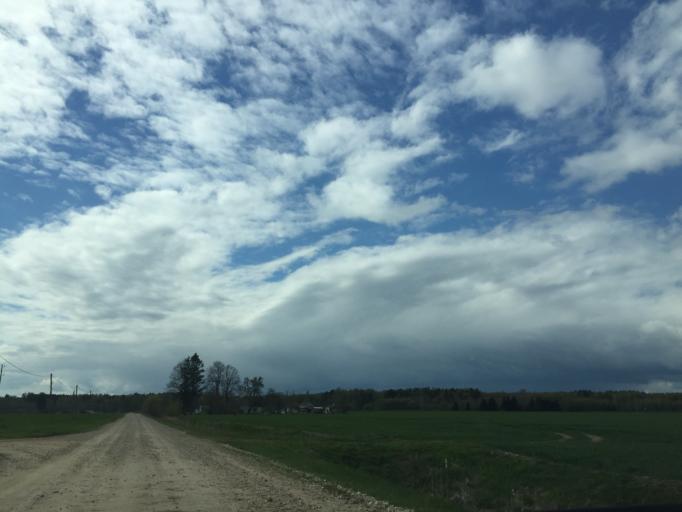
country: LV
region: Ozolnieku
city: Ozolnieki
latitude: 56.5834
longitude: 23.8113
